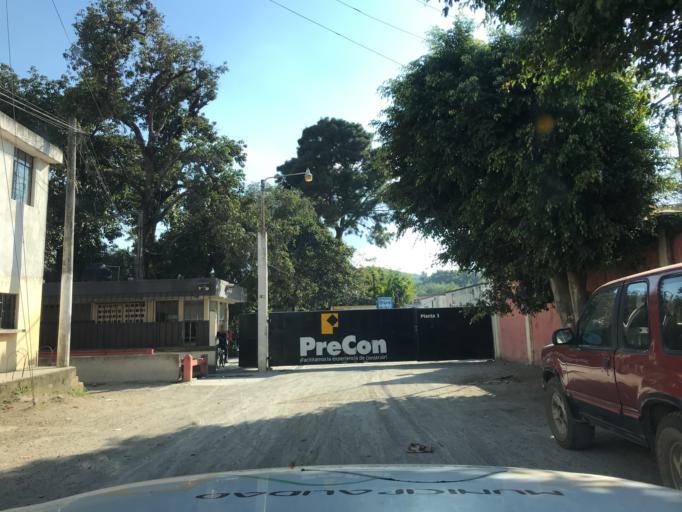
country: GT
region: Guatemala
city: Petapa
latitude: 14.4935
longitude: -90.5575
